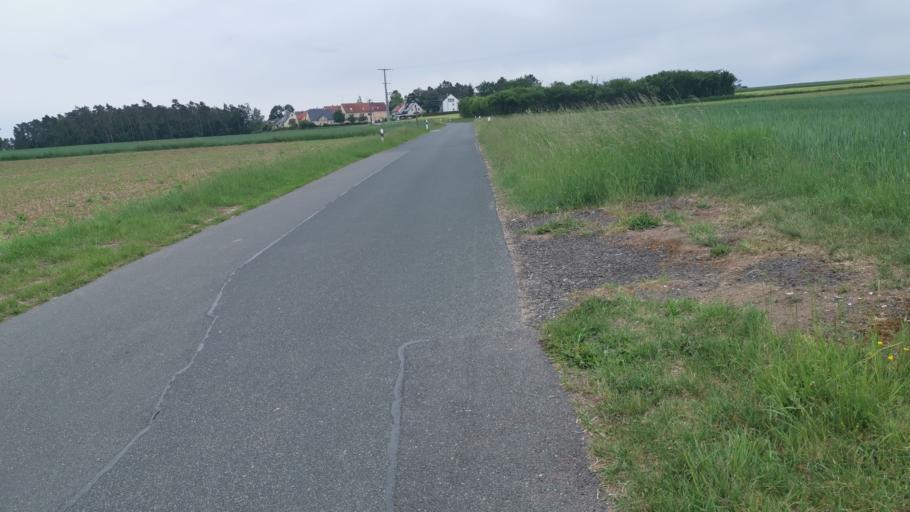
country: DE
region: Bavaria
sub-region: Regierungsbezirk Mittelfranken
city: Schwabach
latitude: 49.3709
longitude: 11.0149
